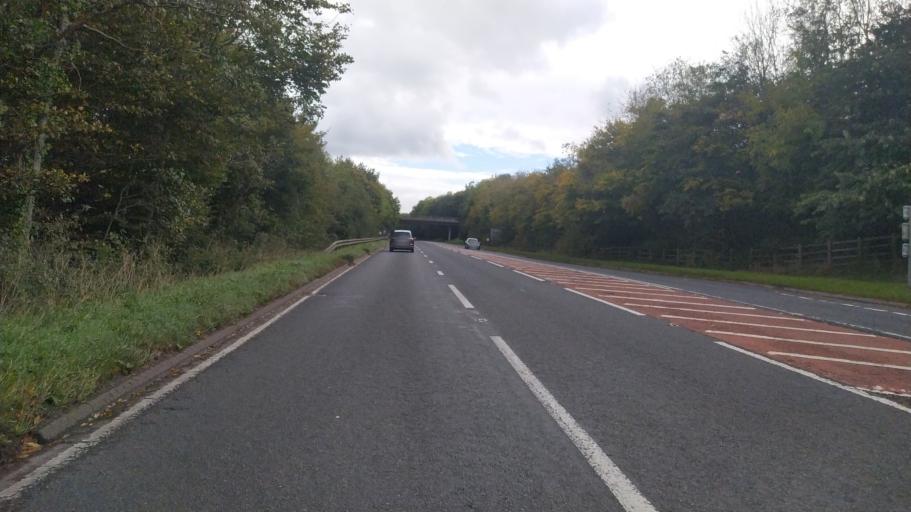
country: GB
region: England
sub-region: Dorset
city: Bridport
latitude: 50.7279
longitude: -2.7781
